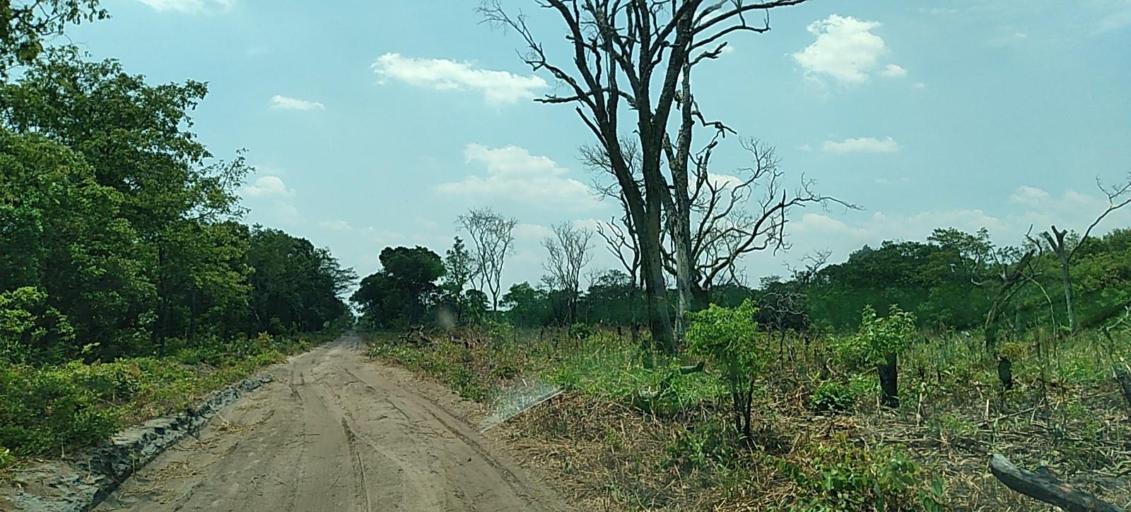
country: CD
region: Katanga
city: Kolwezi
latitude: -11.3124
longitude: 25.2360
